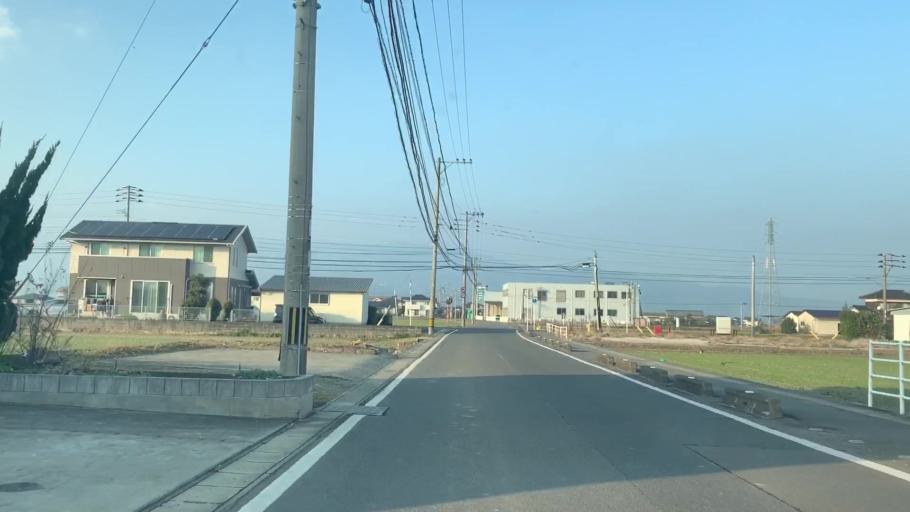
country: JP
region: Saga Prefecture
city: Saga-shi
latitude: 33.2661
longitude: 130.2306
